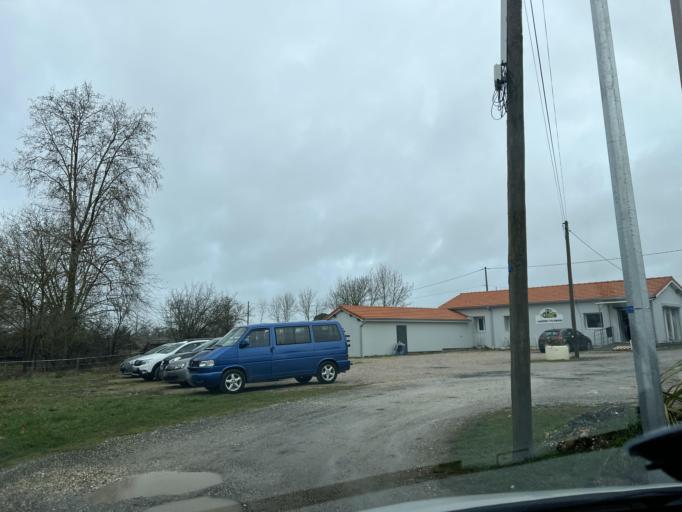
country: FR
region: Aquitaine
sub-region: Departement de la Gironde
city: Gaillan-en-Medoc
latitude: 45.3539
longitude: -0.9822
